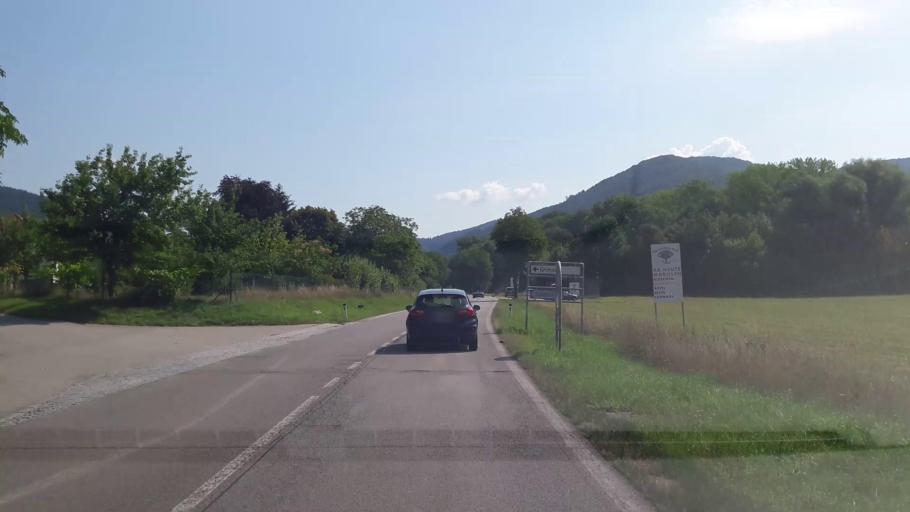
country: AT
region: Lower Austria
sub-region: Politischer Bezirk Melk
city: Emmersdorf an der Donau
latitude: 48.2612
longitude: 15.3641
